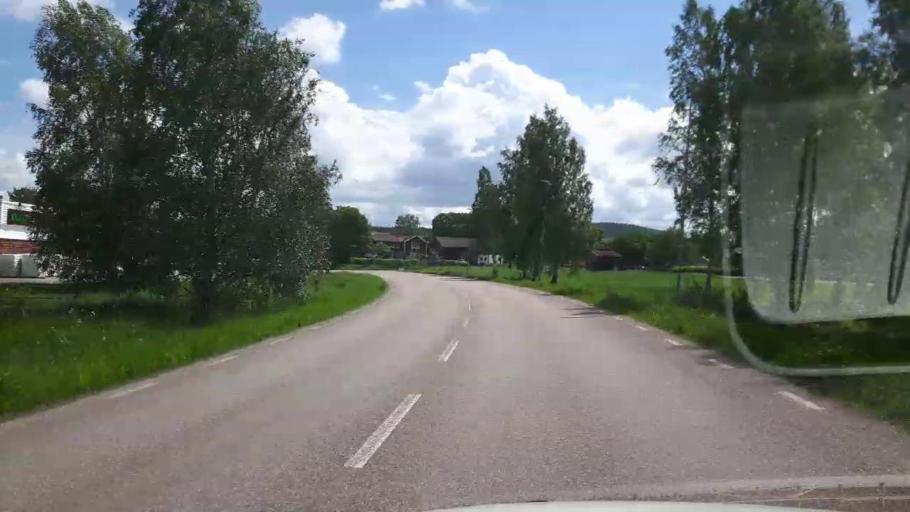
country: SE
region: Dalarna
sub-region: Faluns Kommun
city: Falun
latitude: 60.6532
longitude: 15.7725
